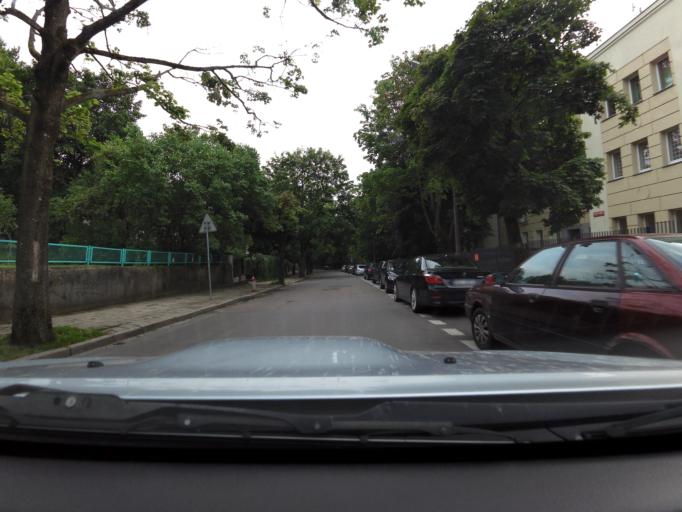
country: PL
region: Warmian-Masurian Voivodeship
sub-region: Powiat olsztynski
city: Olsztyn
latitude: 53.7756
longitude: 20.4850
